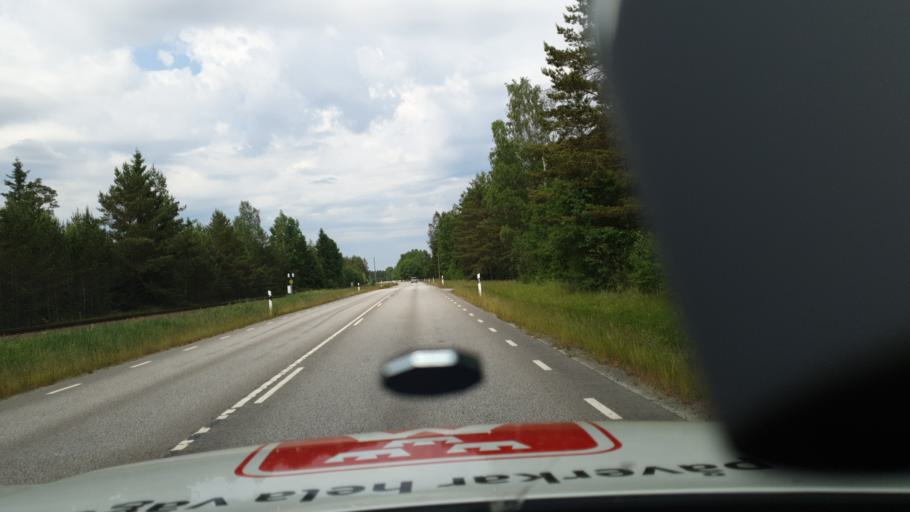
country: SE
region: Joenkoeping
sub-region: Varnamo Kommun
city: Varnamo
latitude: 57.2396
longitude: 14.0437
